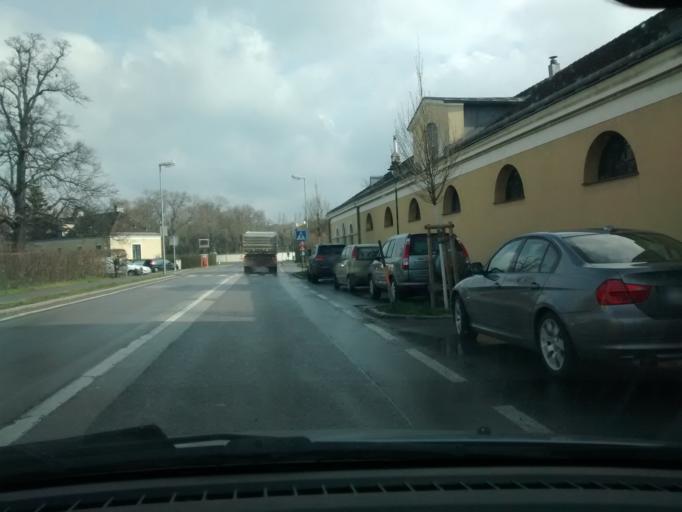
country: AT
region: Lower Austria
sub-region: Politischer Bezirk Modling
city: Laxenburg
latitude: 48.0643
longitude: 16.3536
